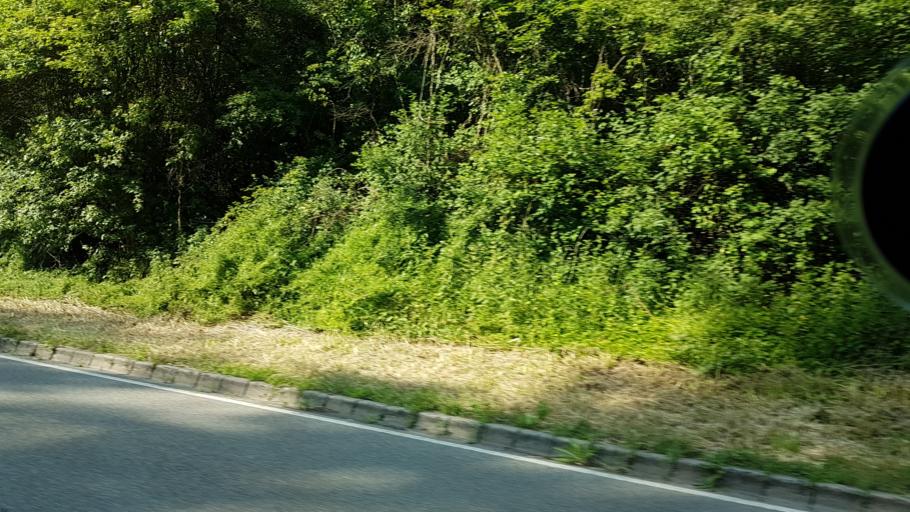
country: DE
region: Rheinland-Pfalz
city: Rathsweiler
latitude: 49.6006
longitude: 7.4822
